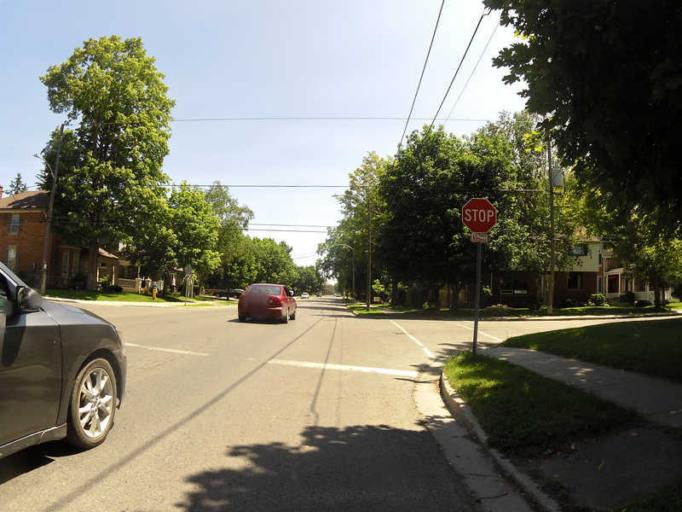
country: CA
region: Ontario
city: Peterborough
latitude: 44.2926
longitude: -78.3170
